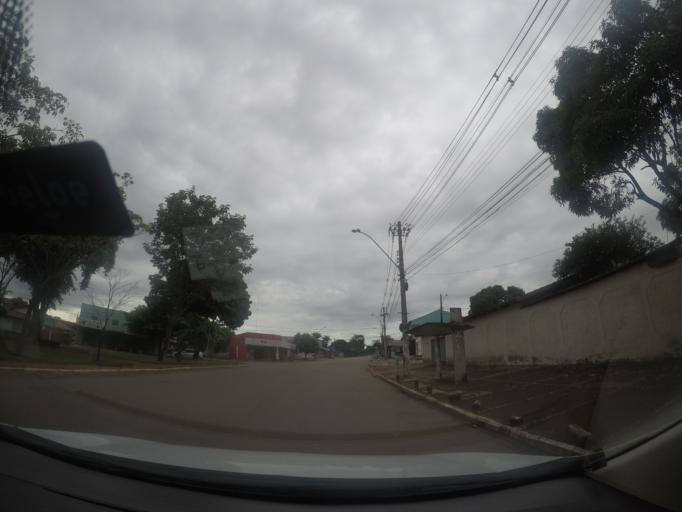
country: BR
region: Goias
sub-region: Goiania
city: Goiania
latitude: -16.6065
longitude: -49.2949
